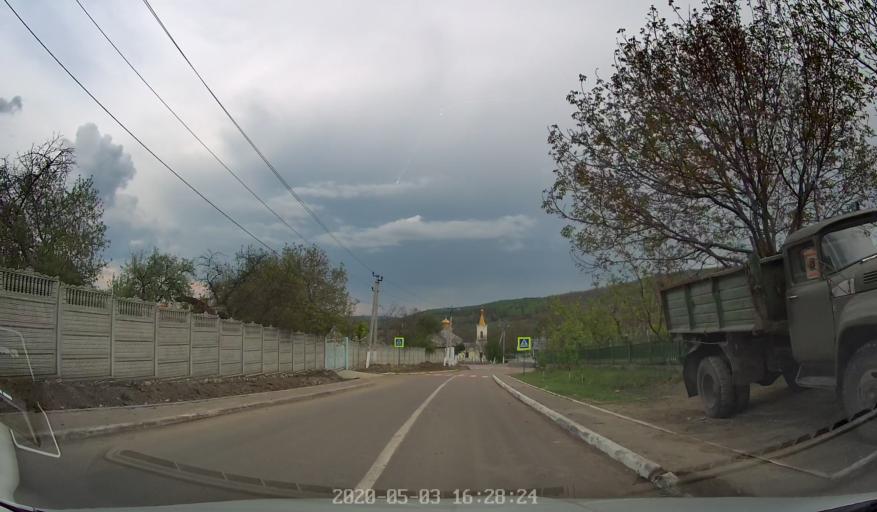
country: MD
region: Calarasi
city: Calarasi
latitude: 47.1934
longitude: 28.3515
